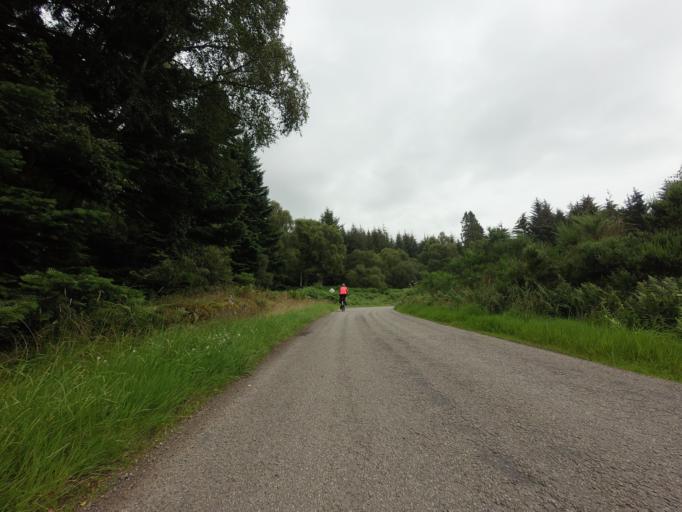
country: GB
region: Scotland
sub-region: Highland
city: Evanton
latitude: 57.8887
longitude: -4.3877
